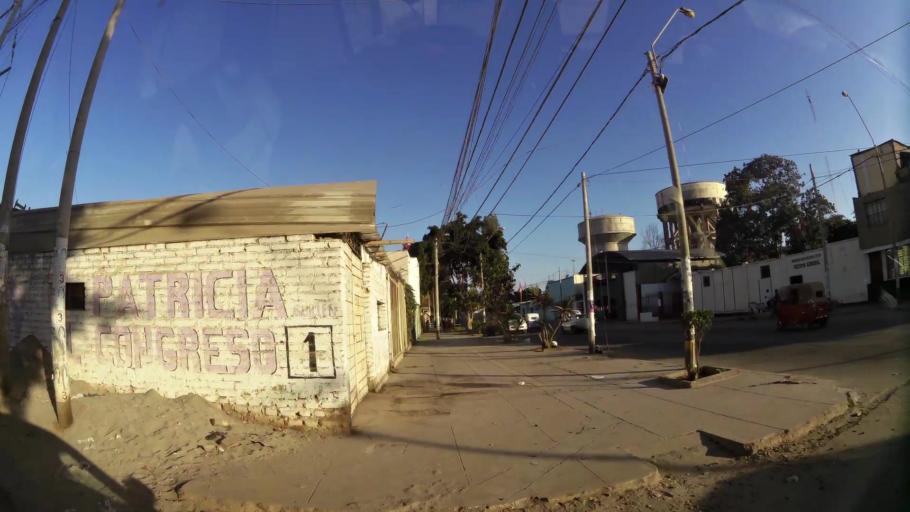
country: PE
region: Ica
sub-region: Provincia de Ica
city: Ica
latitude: -14.0580
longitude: -75.7291
